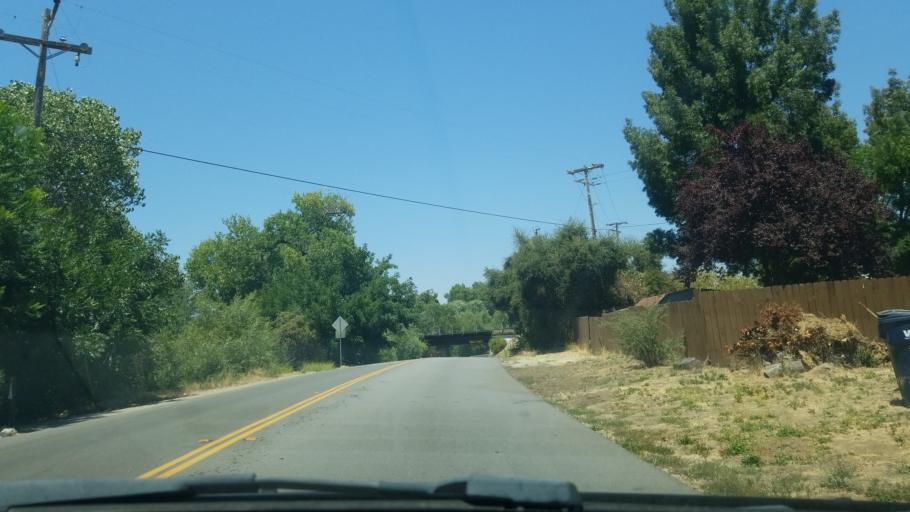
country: US
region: California
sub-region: San Luis Obispo County
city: Atascadero
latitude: 35.4999
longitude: -120.6621
